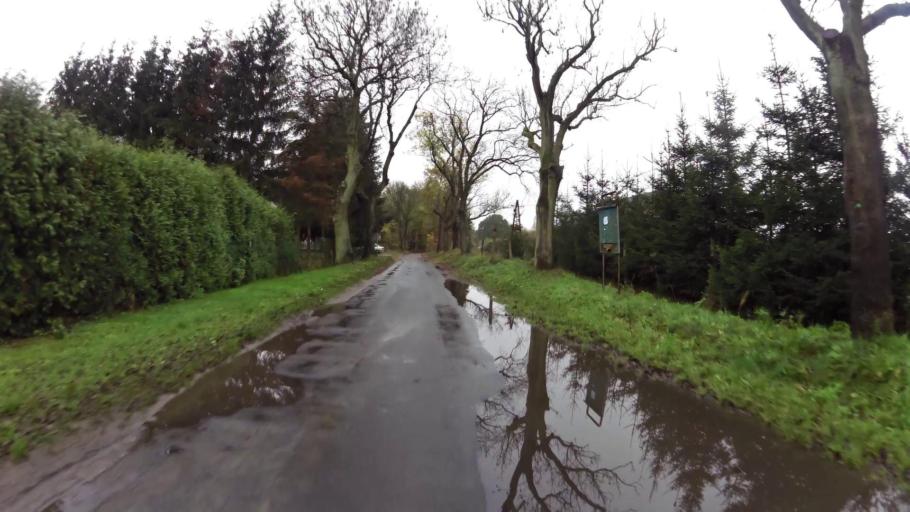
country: PL
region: West Pomeranian Voivodeship
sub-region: Powiat gryfinski
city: Gryfino
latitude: 53.2286
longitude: 14.5236
